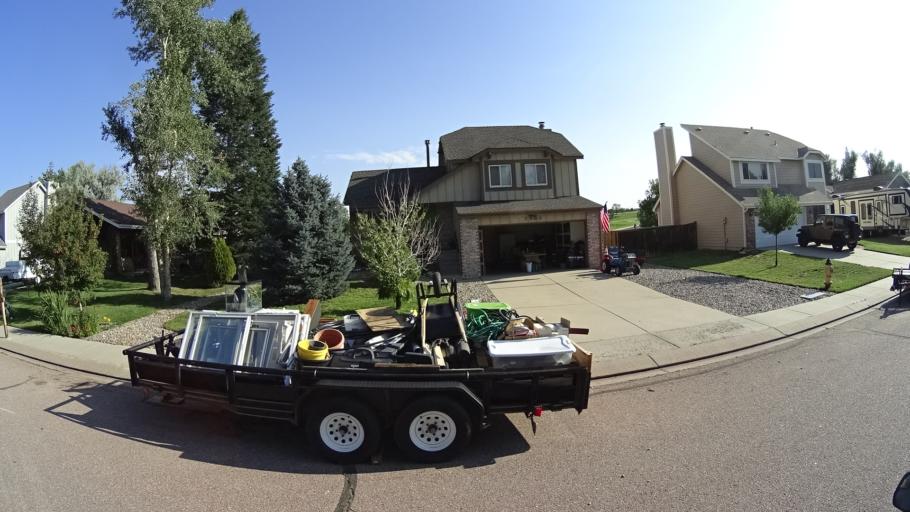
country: US
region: Colorado
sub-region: El Paso County
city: Black Forest
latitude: 38.9459
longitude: -104.7683
